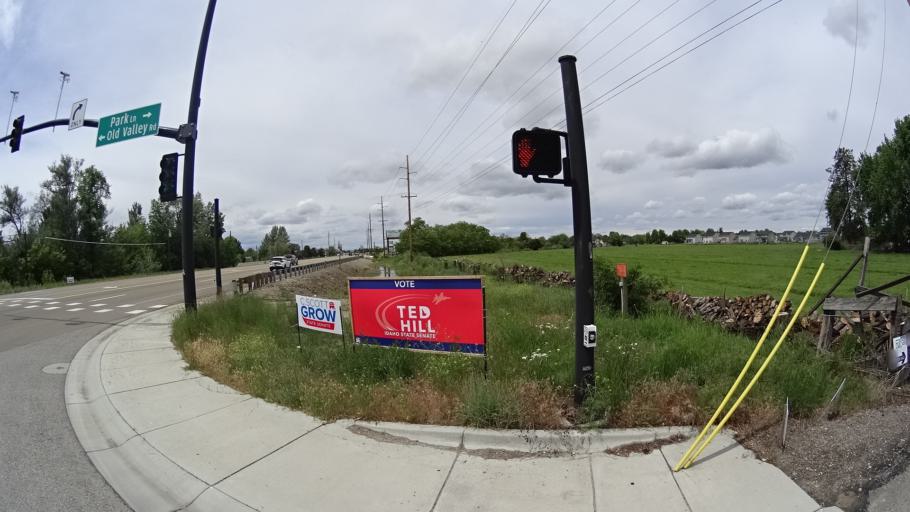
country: US
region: Idaho
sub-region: Ada County
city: Eagle
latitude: 43.6954
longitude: -116.4036
